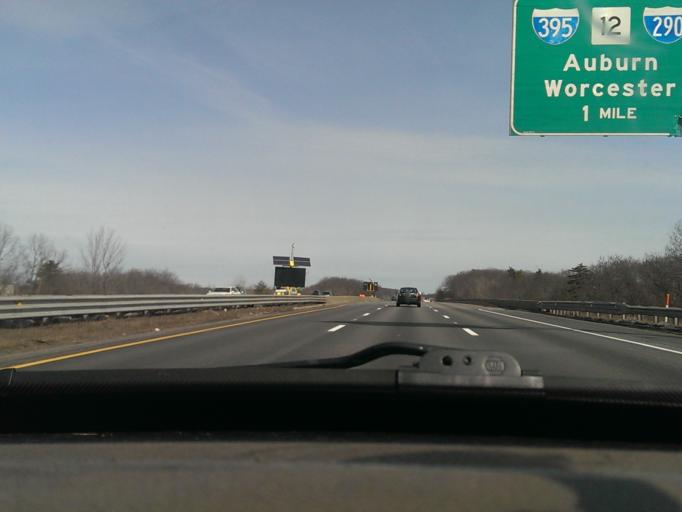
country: US
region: Massachusetts
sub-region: Worcester County
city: Auburn
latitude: 42.1877
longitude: -71.8734
